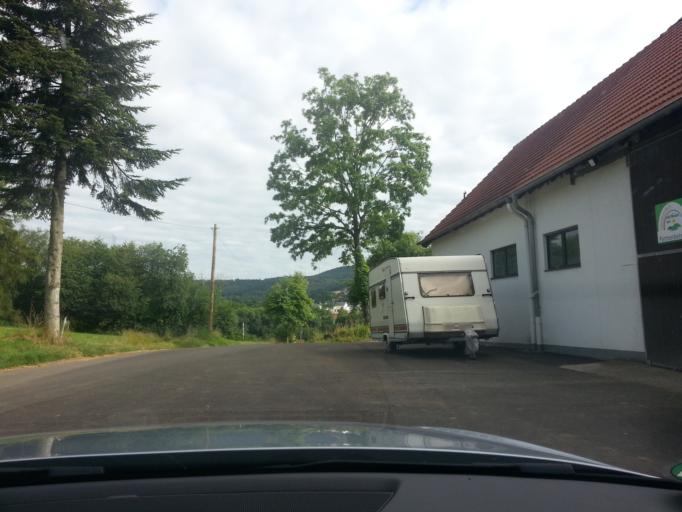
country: DE
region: Saarland
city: Oberthal
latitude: 49.5049
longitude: 7.0823
